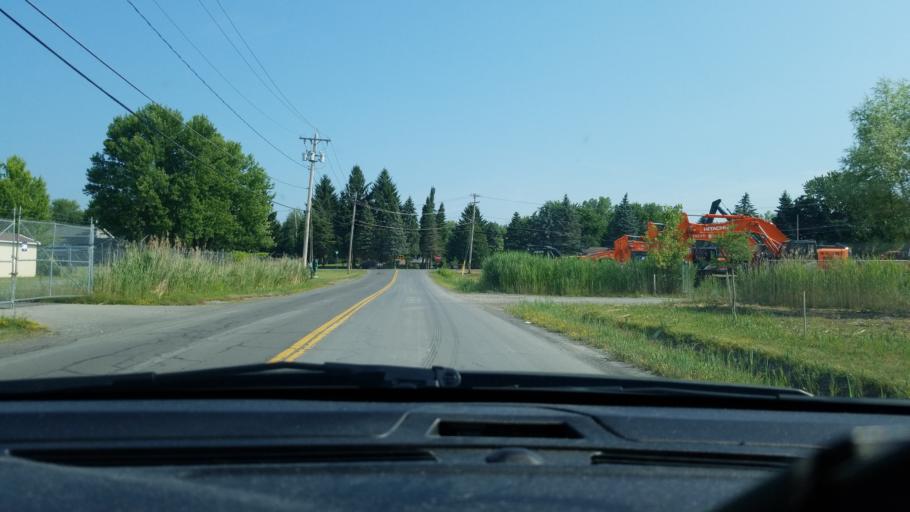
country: US
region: New York
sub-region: Onondaga County
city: North Syracuse
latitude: 43.1265
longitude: -76.0734
